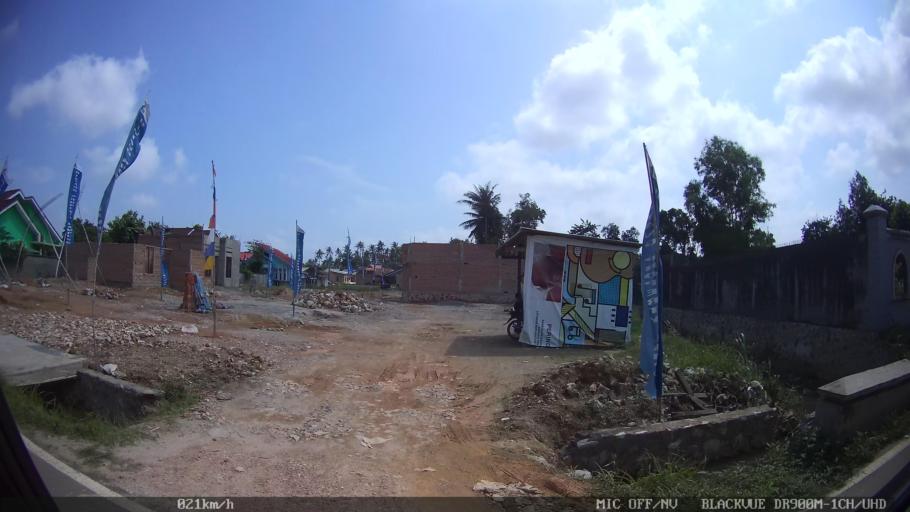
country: ID
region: Lampung
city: Kedaton
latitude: -5.3495
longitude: 105.2837
